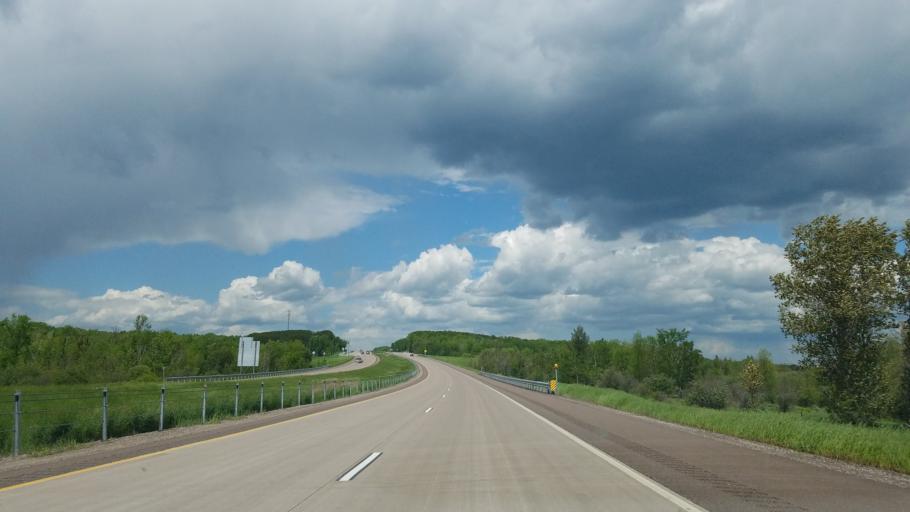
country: US
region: Minnesota
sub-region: Carlton County
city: Moose Lake
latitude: 46.4486
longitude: -92.7339
